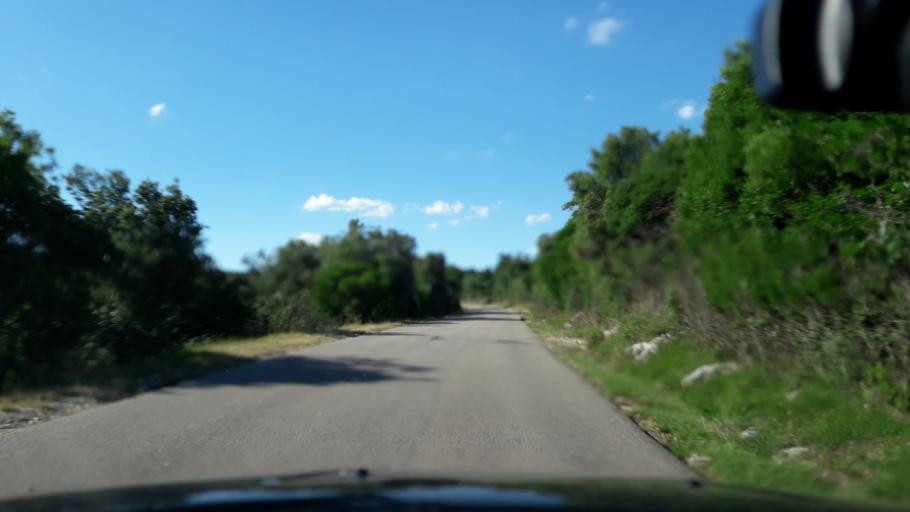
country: FR
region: Languedoc-Roussillon
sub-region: Departement du Gard
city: Saint-Julien-de-Peyrolas
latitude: 44.3672
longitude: 4.5224
